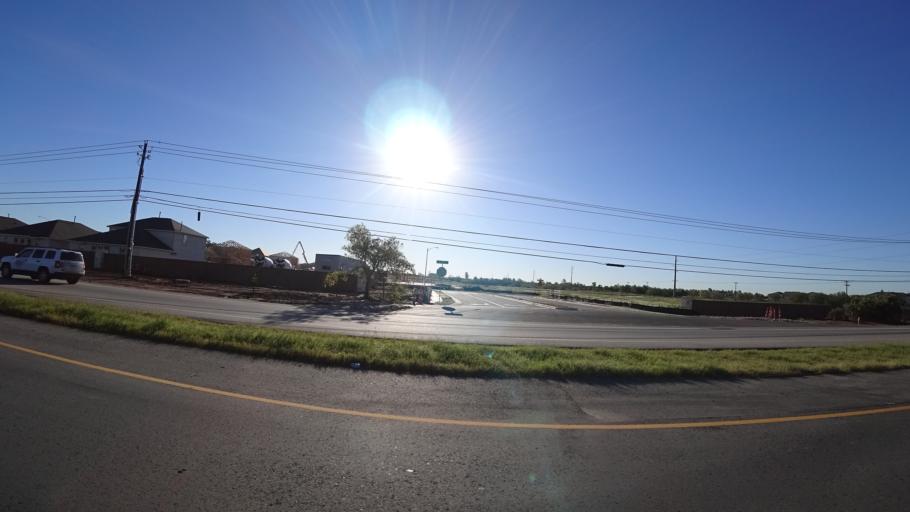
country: US
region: Texas
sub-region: Travis County
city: Hornsby Bend
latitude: 30.2184
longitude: -97.6364
